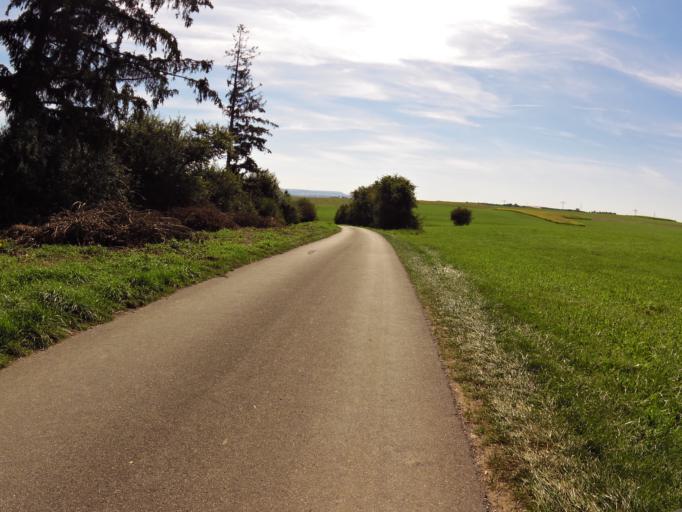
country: DE
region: Baden-Wuerttemberg
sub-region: Freiburg Region
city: Bad Durrheim
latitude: 48.0144
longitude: 8.4976
